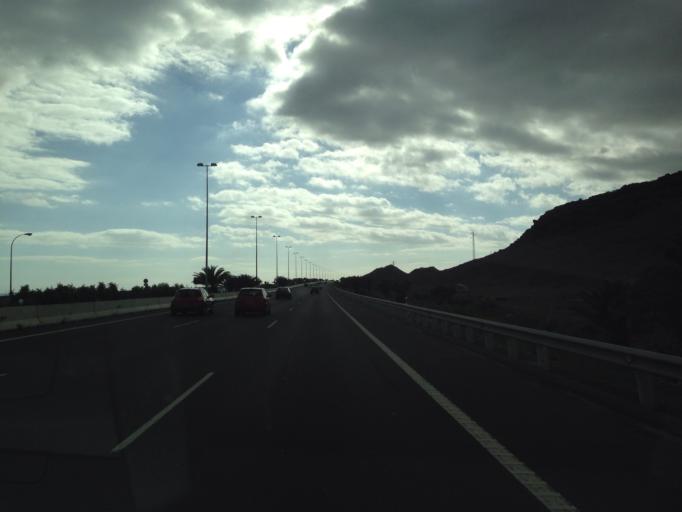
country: ES
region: Canary Islands
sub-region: Provincia de Las Palmas
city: Cruce de Arinaga
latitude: 27.8035
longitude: -15.4839
